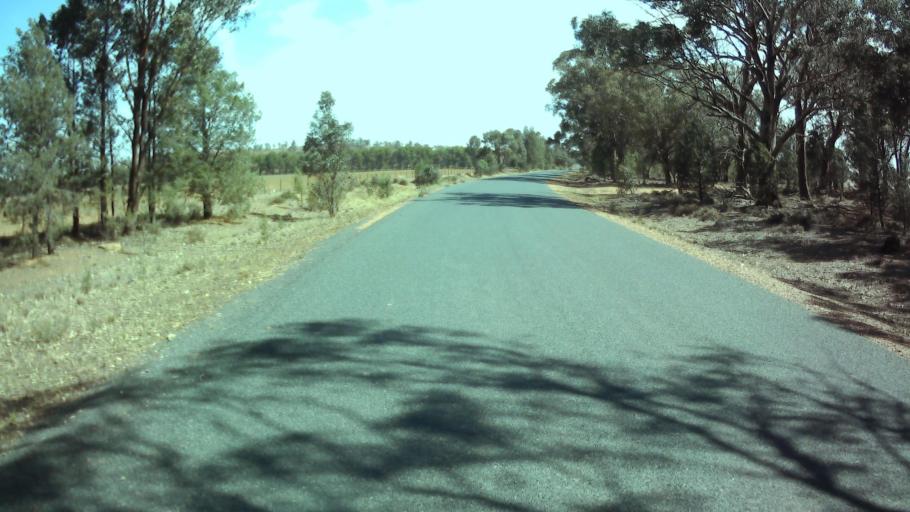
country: AU
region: New South Wales
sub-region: Weddin
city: Grenfell
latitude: -34.0384
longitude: 148.1346
